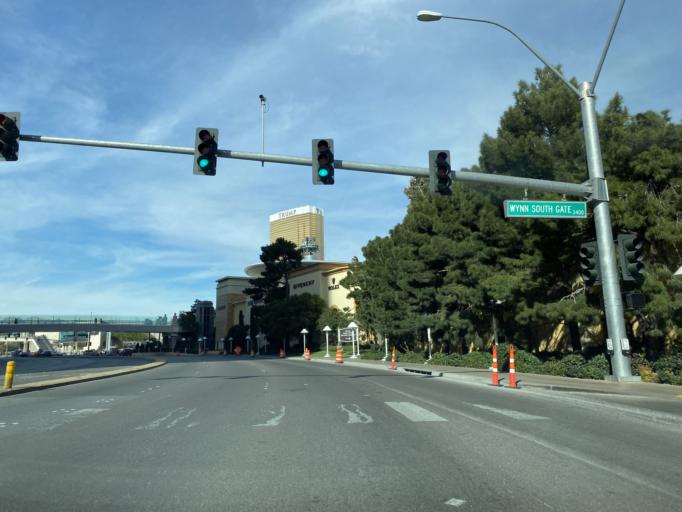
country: US
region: Nevada
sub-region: Clark County
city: Paradise
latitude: 36.1248
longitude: -115.1670
